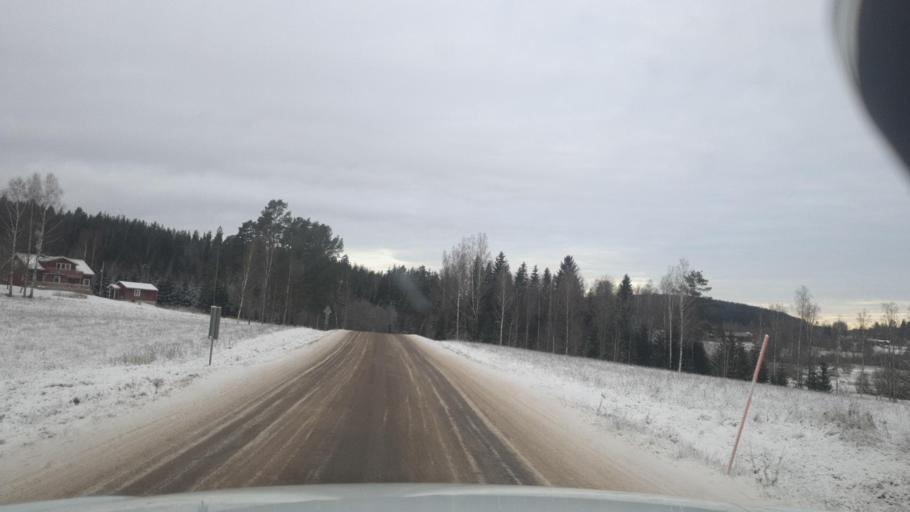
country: SE
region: Vaermland
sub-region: Arvika Kommun
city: Arvika
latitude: 59.6286
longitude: 12.8014
